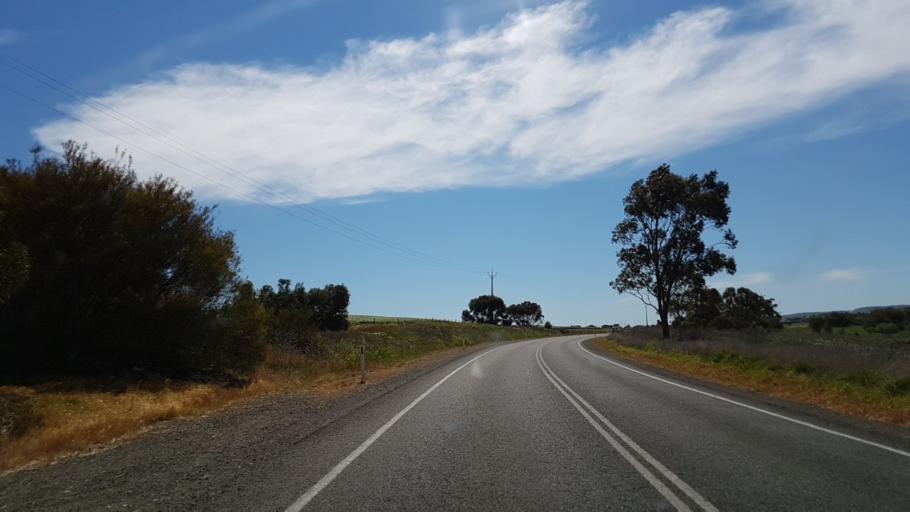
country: AU
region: South Australia
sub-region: Light
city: Kapunda
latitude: -34.1324
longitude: 138.7498
